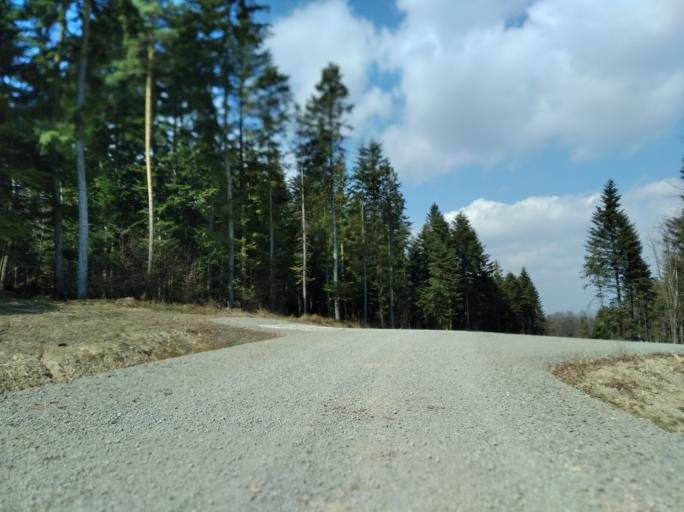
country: PL
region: Subcarpathian Voivodeship
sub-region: Powiat strzyzowski
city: Strzyzow
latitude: 49.8222
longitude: 21.8012
